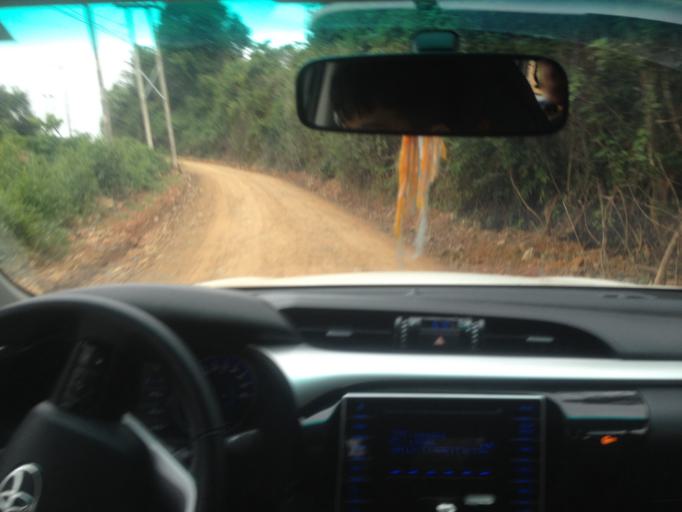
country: TH
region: Nan
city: Chaloem Phra Kiat
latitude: 19.9720
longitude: 101.1364
